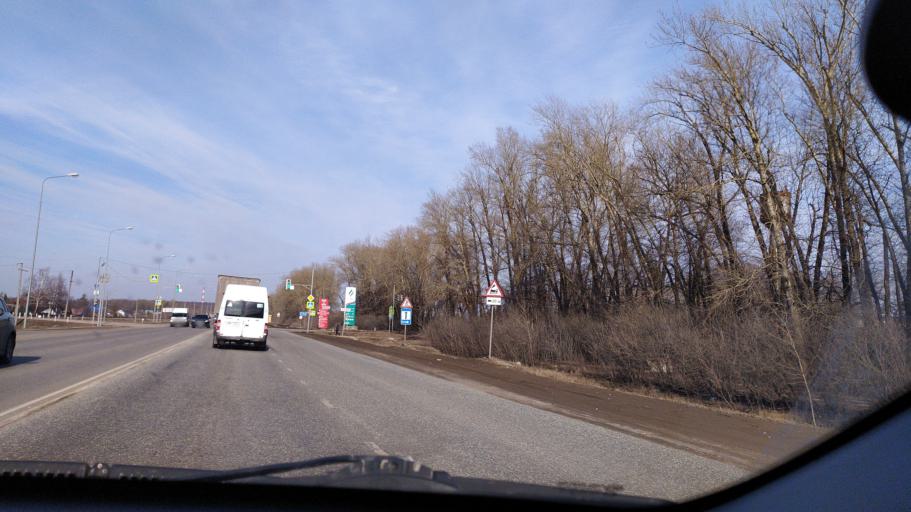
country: RU
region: Chuvashia
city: Novyye Lapsary
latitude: 56.0764
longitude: 47.2240
